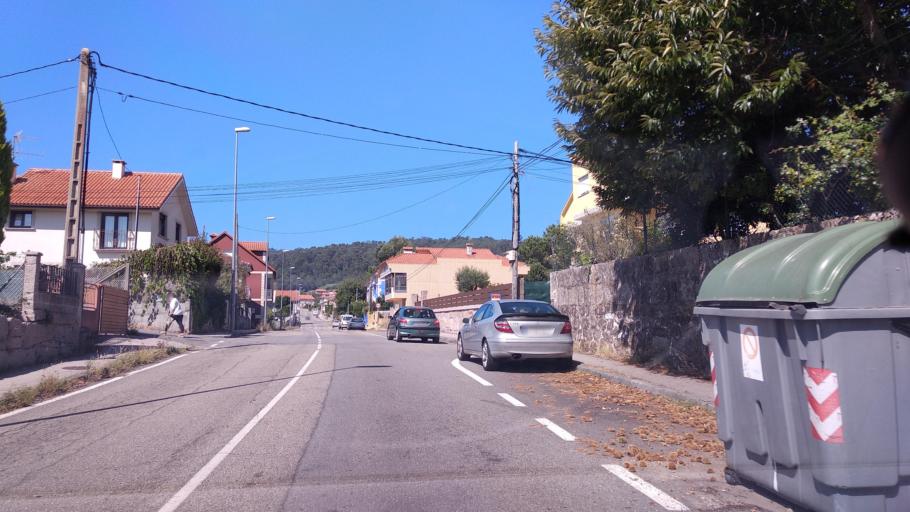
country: ES
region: Galicia
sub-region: Provincia de Pontevedra
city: Cangas
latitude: 42.2711
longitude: -8.7677
